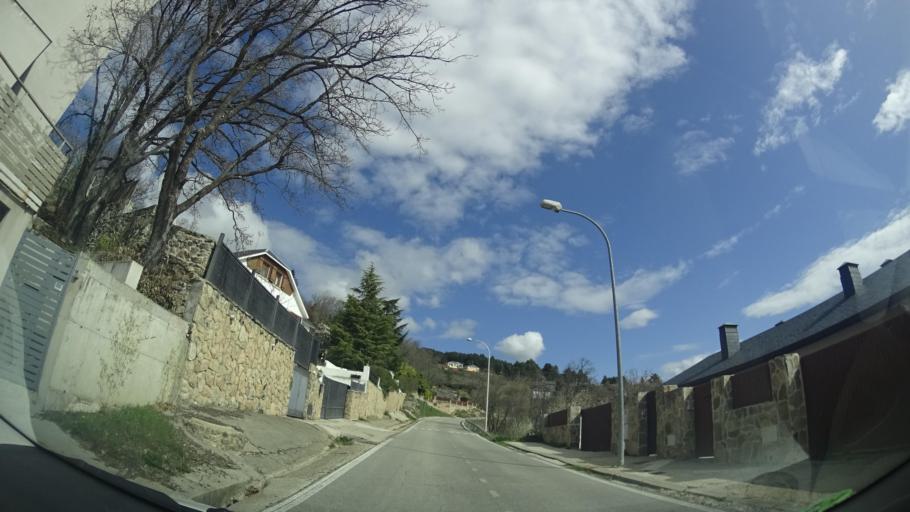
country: ES
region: Madrid
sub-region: Provincia de Madrid
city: Miraflores de la Sierra
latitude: 40.8185
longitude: -3.7631
